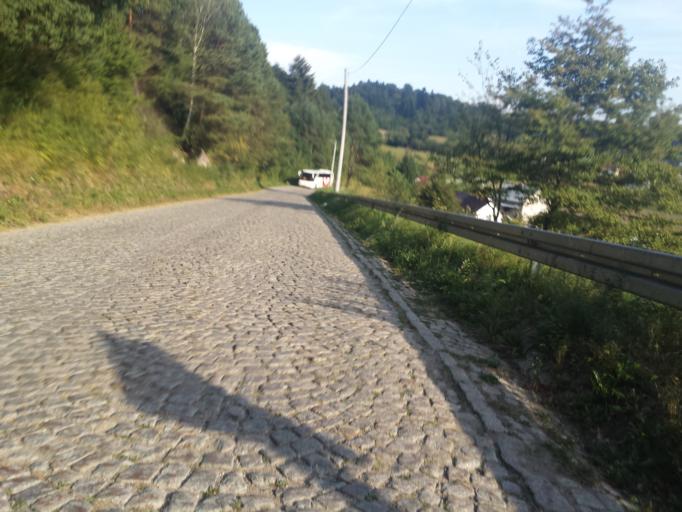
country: PL
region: Subcarpathian Voivodeship
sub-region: Powiat leski
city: Uherce Mineralne
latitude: 49.4431
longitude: 22.4063
